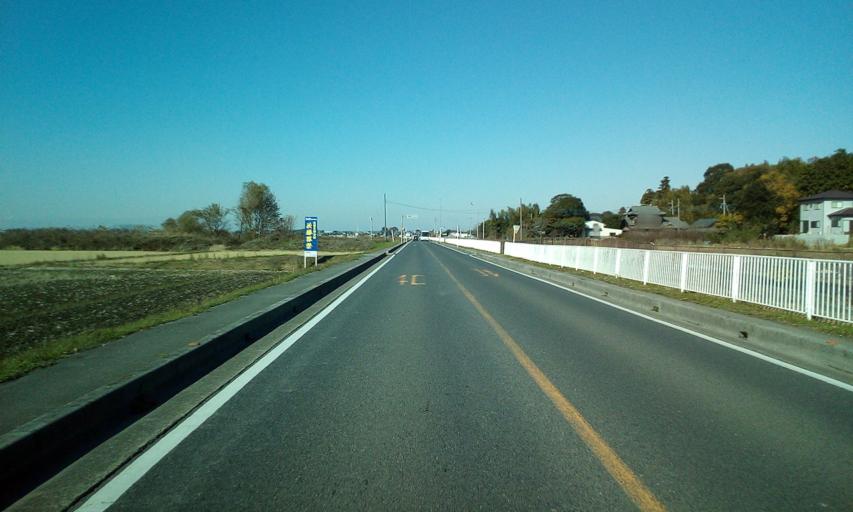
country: JP
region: Chiba
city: Noda
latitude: 35.9590
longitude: 139.8251
